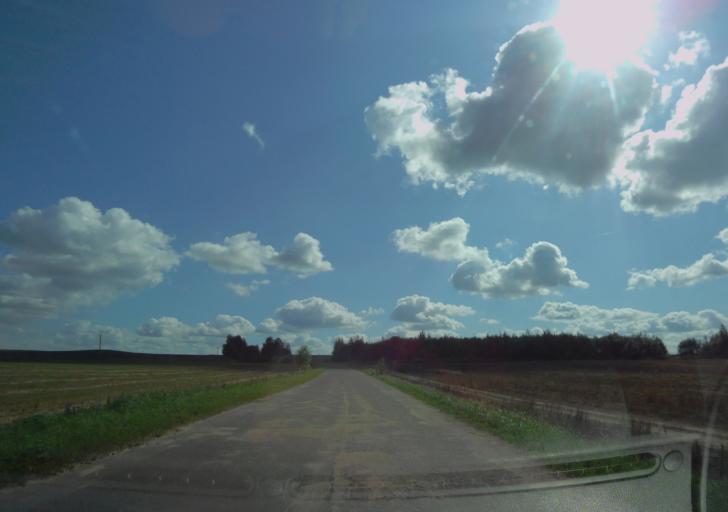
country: BY
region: Minsk
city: Zyembin
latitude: 54.4090
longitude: 28.3892
